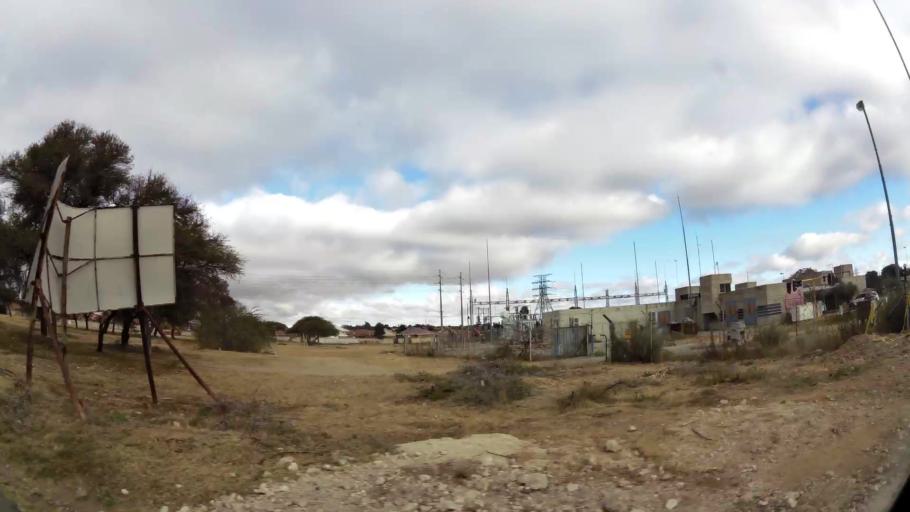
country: ZA
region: Limpopo
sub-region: Capricorn District Municipality
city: Polokwane
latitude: -23.9215
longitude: 29.4525
